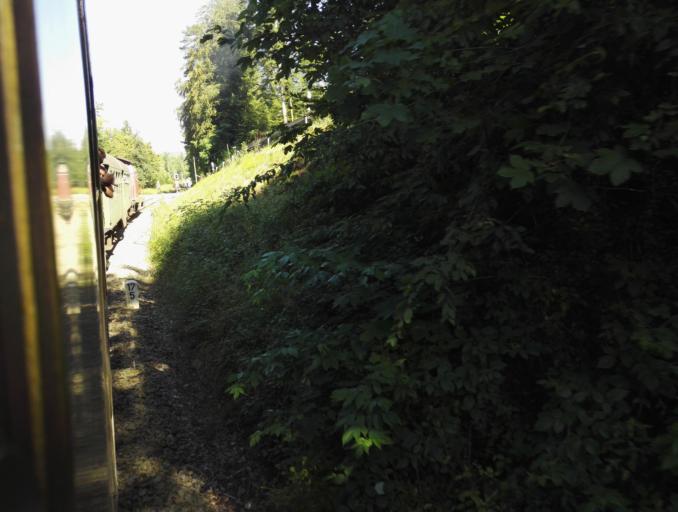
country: DE
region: Baden-Wuerttemberg
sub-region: Regierungsbezirk Stuttgart
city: Welzheim
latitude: 48.8803
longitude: 9.6083
